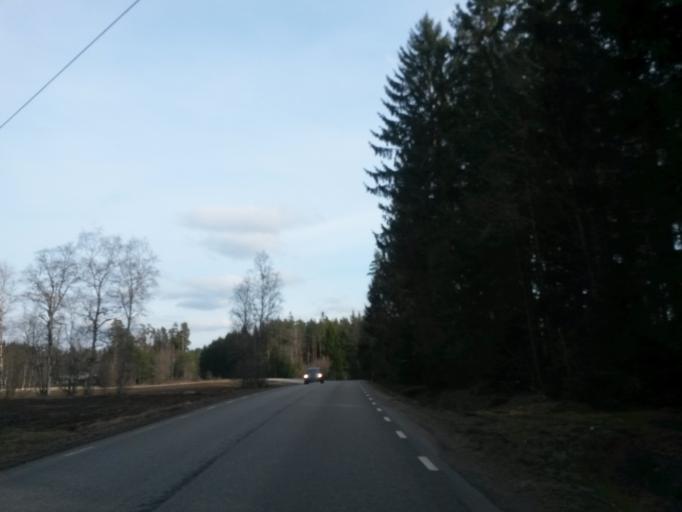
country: SE
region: Vaestra Goetaland
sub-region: Vargarda Kommun
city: Jonstorp
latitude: 57.9831
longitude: 12.7297
